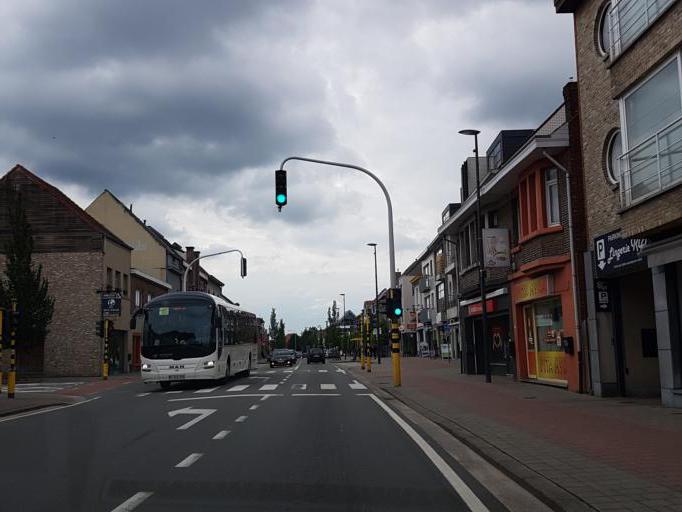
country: BE
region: Flanders
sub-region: Provincie Antwerpen
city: Zoersel
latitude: 51.2971
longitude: 4.6903
